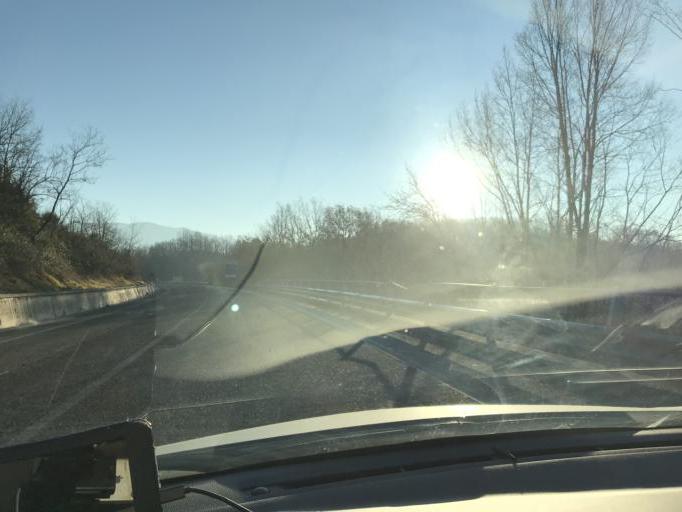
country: IT
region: Latium
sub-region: Provincia di Rieti
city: Fiamignano
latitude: 42.2572
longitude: 13.1253
